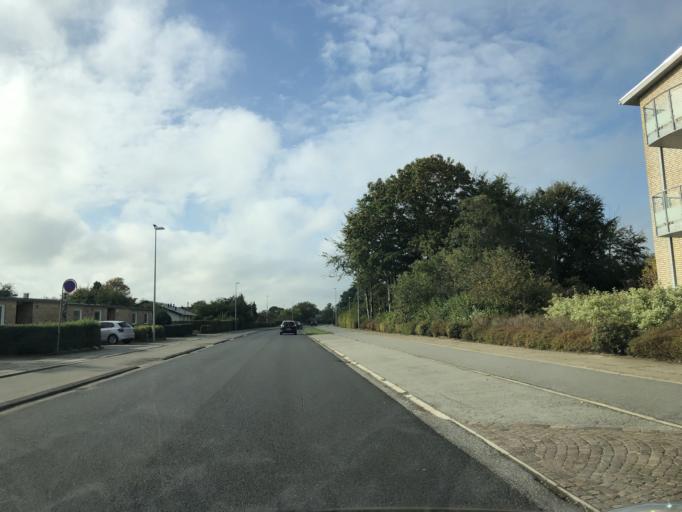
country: DK
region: Central Jutland
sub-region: Holstebro Kommune
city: Holstebro
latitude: 56.3657
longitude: 8.6033
